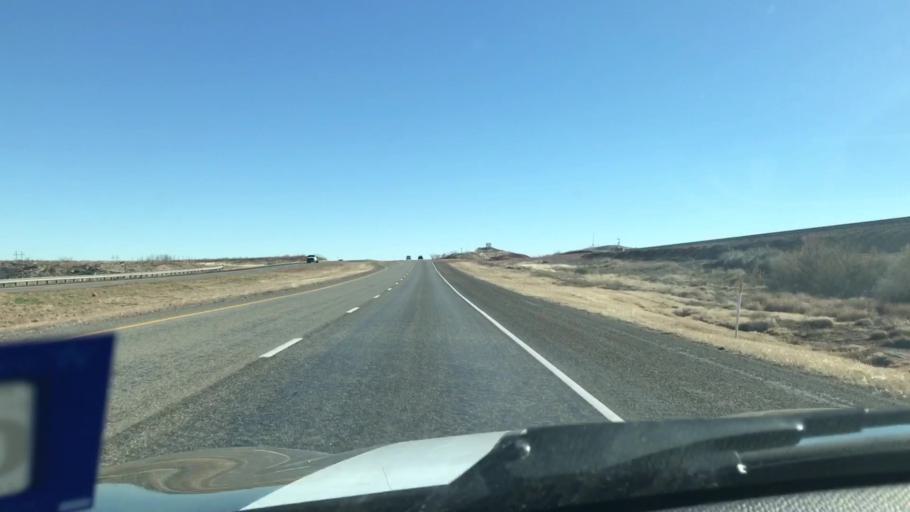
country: US
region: Texas
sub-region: Garza County
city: Post
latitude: 33.1116
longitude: -101.2716
